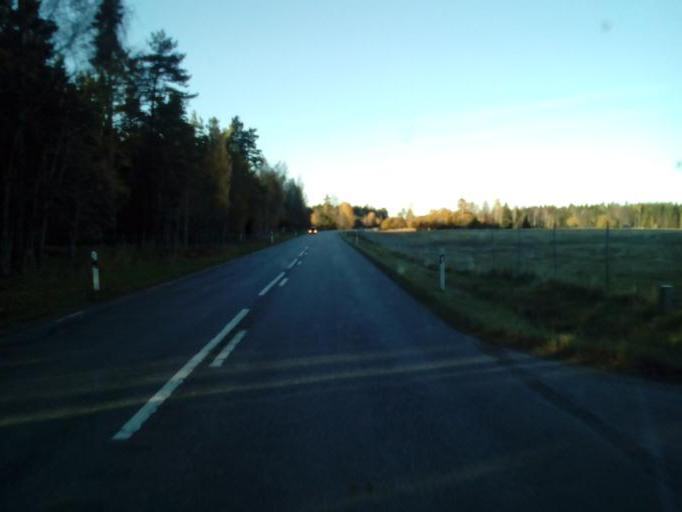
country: SE
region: OErebro
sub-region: Hallsbergs Kommun
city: Palsboda
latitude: 58.9821
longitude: 15.4094
